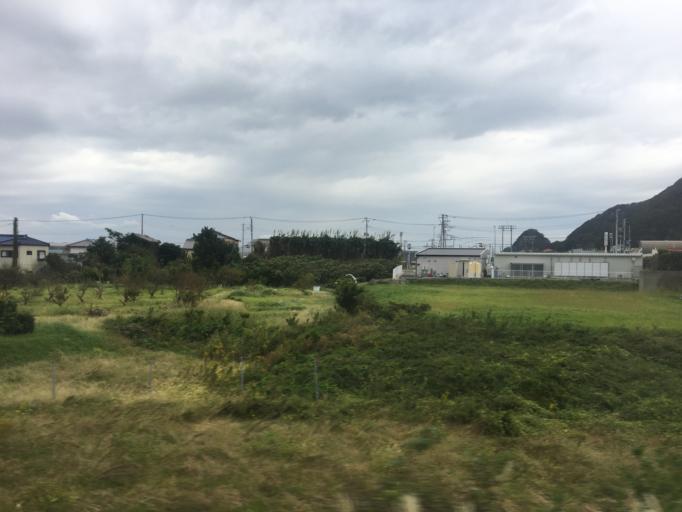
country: JP
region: Chiba
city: Tateyama
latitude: 35.0981
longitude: 139.8490
